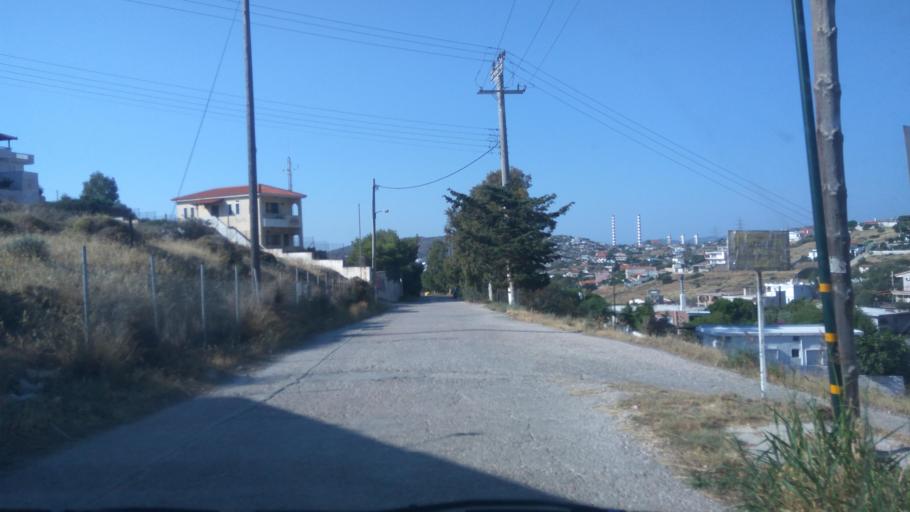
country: GR
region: Attica
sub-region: Nomarchia Anatolikis Attikis
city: Lavrio
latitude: 37.7670
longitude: 24.0743
